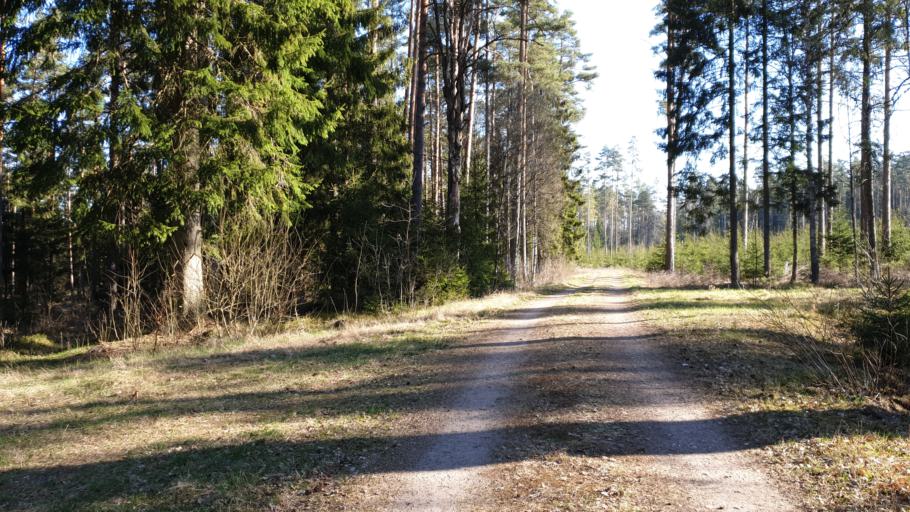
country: SE
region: Kronoberg
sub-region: Ljungby Kommun
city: Ljungby
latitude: 56.8323
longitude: 13.9027
